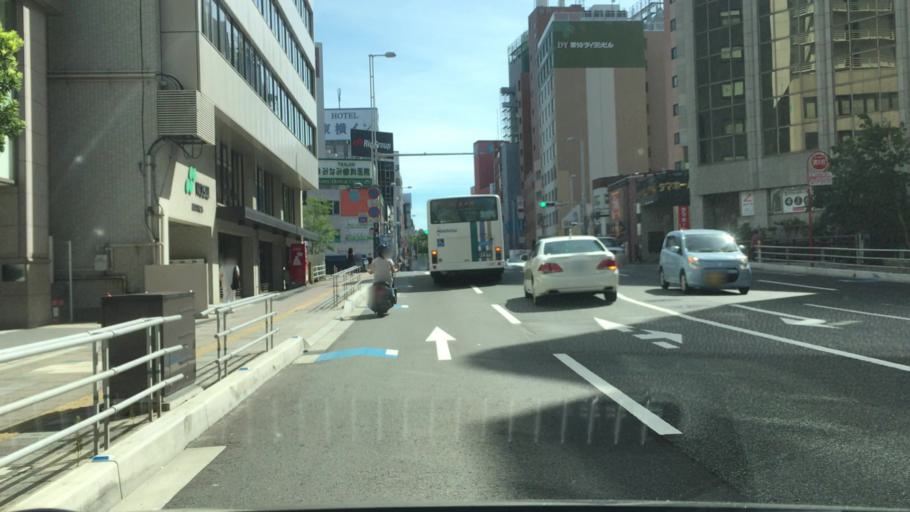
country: JP
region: Fukuoka
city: Fukuoka-shi
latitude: 33.5889
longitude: 130.4030
